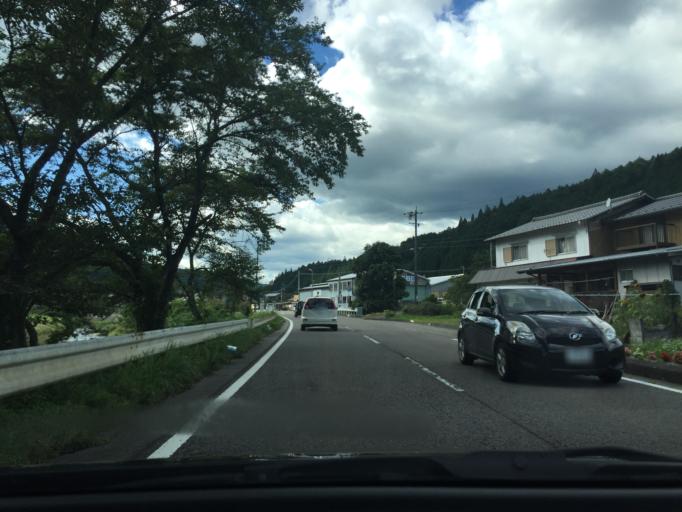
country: JP
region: Gifu
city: Nakatsugawa
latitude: 35.7196
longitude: 137.3617
